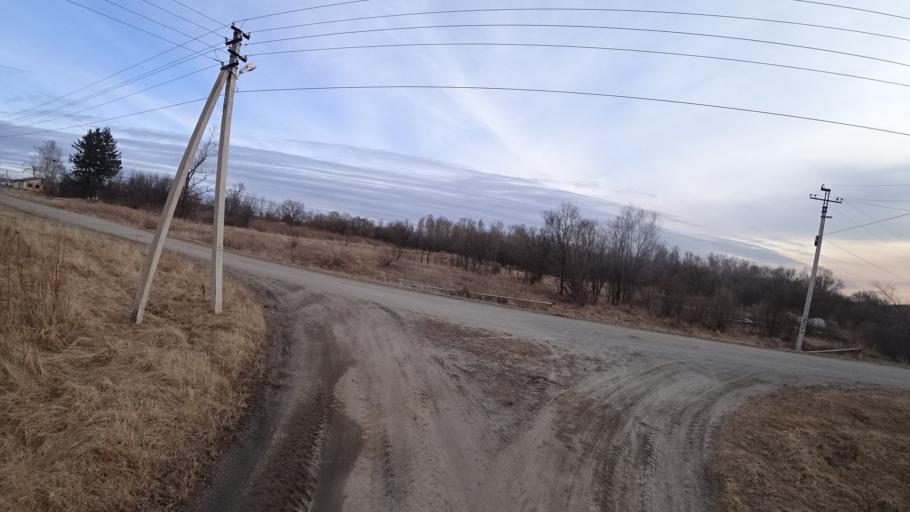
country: RU
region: Amur
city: Bureya
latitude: 50.0209
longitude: 129.7656
